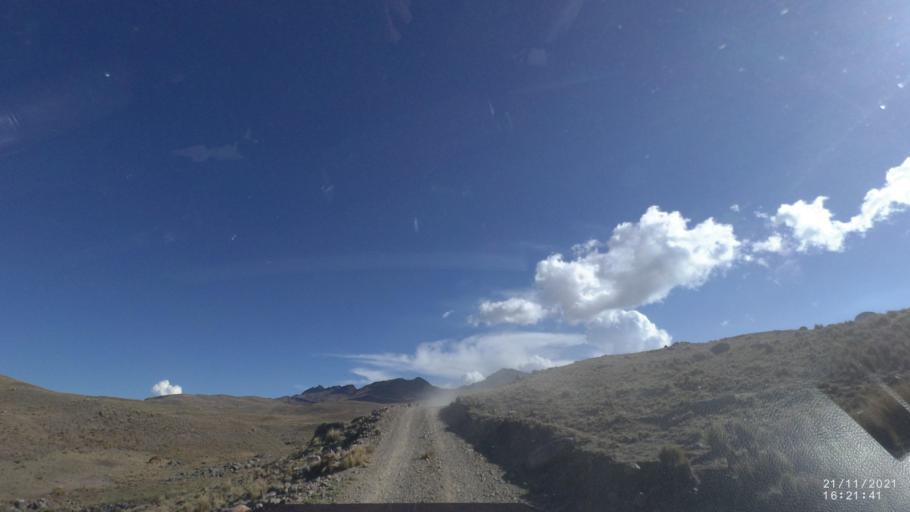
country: BO
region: Cochabamba
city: Cochabamba
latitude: -17.0161
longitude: -66.2854
